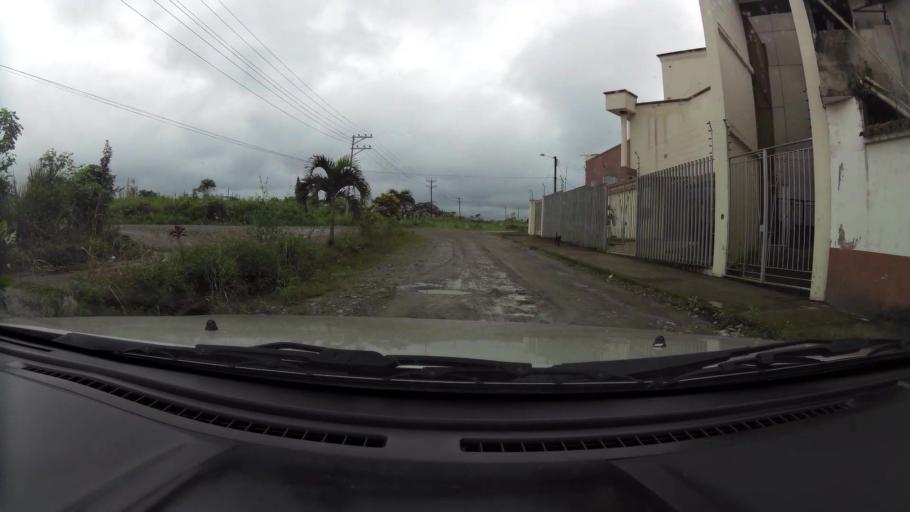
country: EC
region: Santo Domingo de los Tsachilas
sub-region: Canton Santo Domingo de los Colorados
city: Santo Domingo de los Colorados
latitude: -0.2501
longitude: -79.1431
